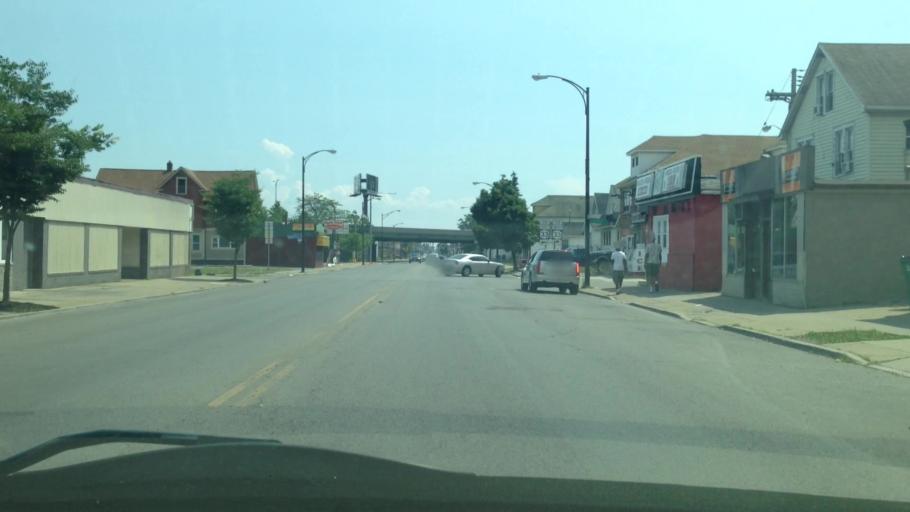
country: US
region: New York
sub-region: Erie County
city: Eggertsville
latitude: 42.9344
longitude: -78.8137
